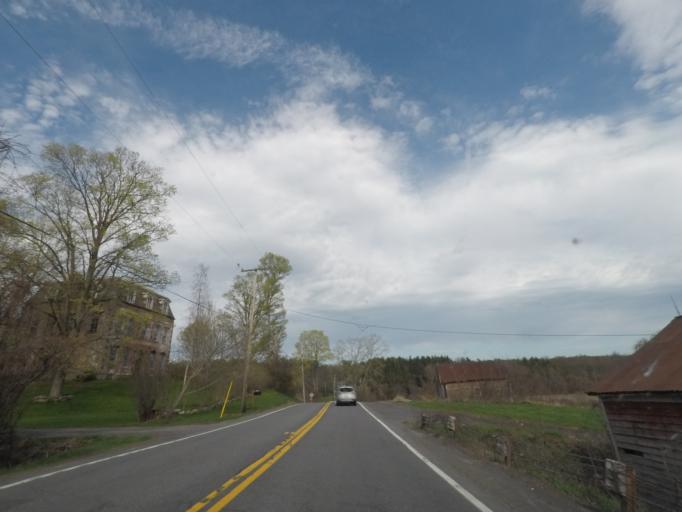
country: US
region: New York
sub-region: Albany County
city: Delmar
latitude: 42.5683
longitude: -73.9035
